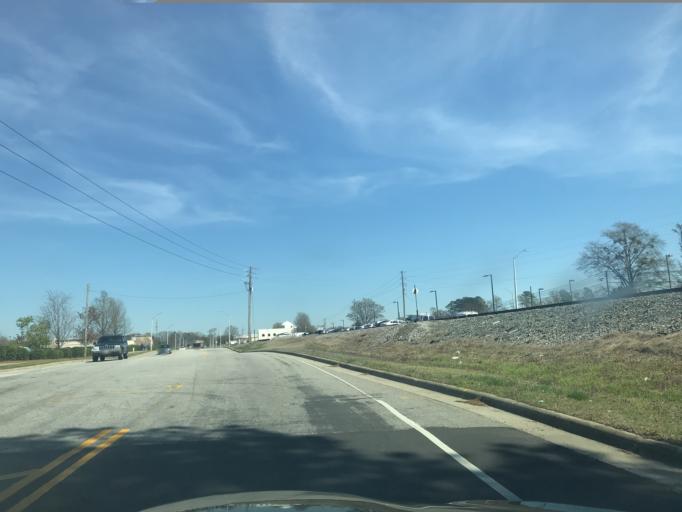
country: US
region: North Carolina
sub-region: Wake County
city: Fuquay-Varina
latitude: 35.5922
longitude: -78.7857
